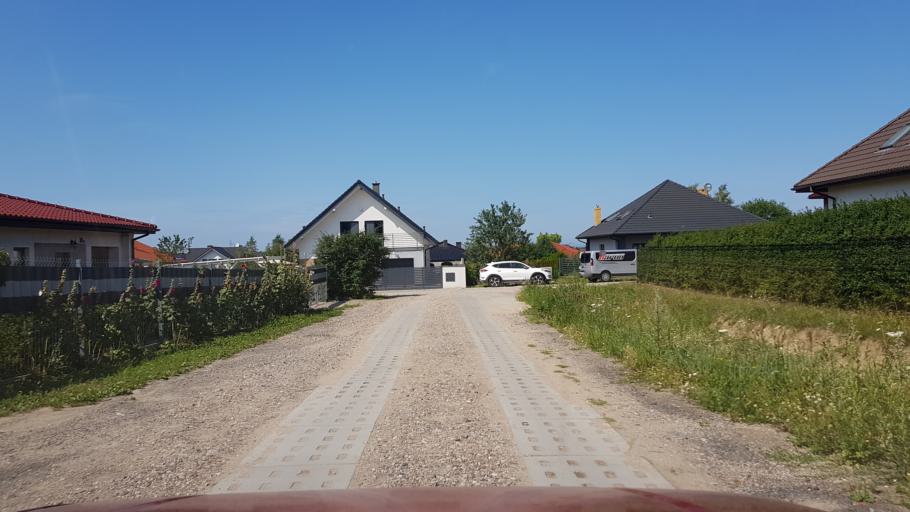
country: PL
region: West Pomeranian Voivodeship
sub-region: Koszalin
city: Koszalin
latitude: 54.2165
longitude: 16.1702
